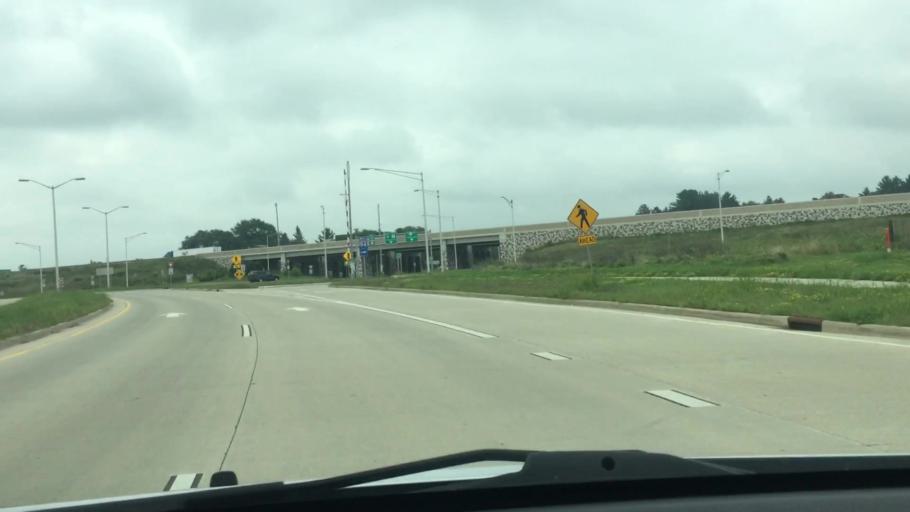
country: US
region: Wisconsin
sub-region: Waukesha County
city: Delafield
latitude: 43.0628
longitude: -88.4434
